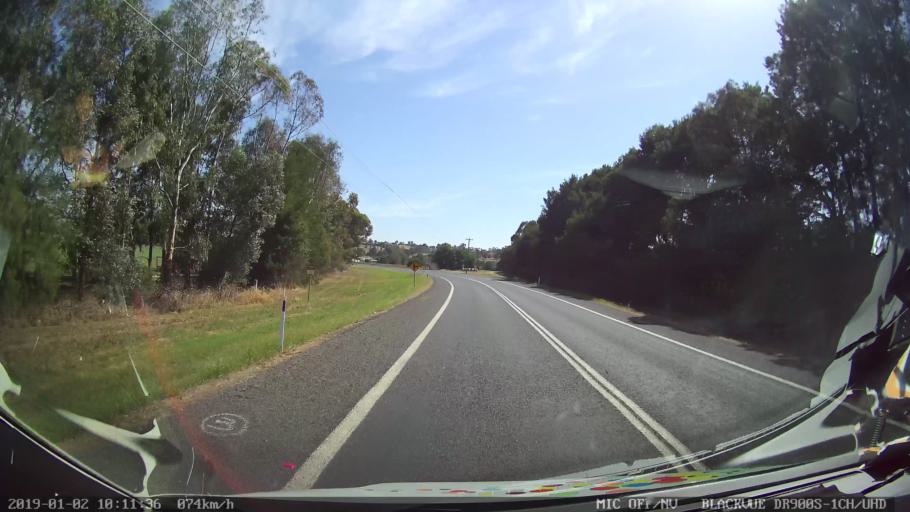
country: AU
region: New South Wales
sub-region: Gundagai
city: Gundagai
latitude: -35.0915
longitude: 148.0936
